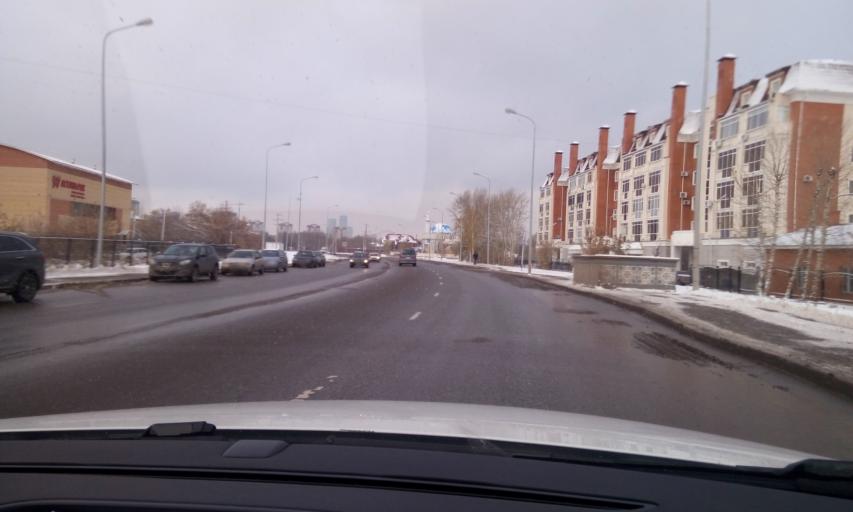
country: KZ
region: Astana Qalasy
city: Astana
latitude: 51.1363
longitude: 71.4356
